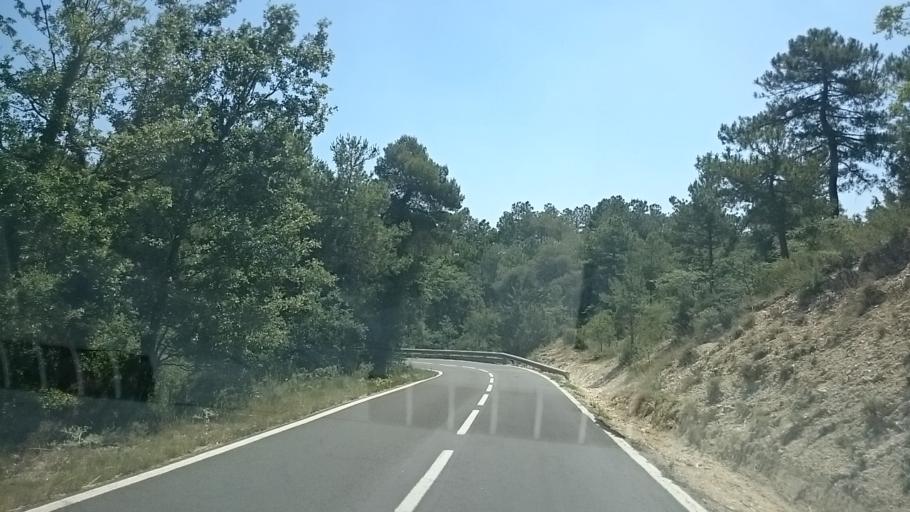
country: ES
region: Catalonia
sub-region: Provincia de Barcelona
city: Bellprat
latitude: 41.4592
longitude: 1.4668
